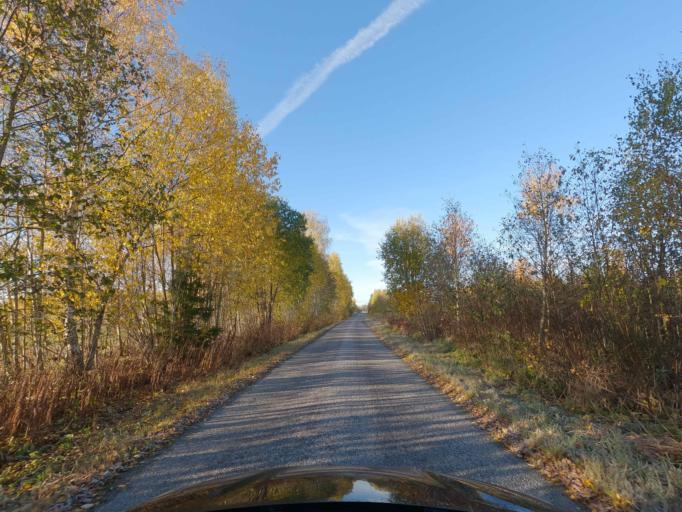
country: EE
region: Raplamaa
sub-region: Rapla vald
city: Rapla
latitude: 59.0599
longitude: 24.8408
